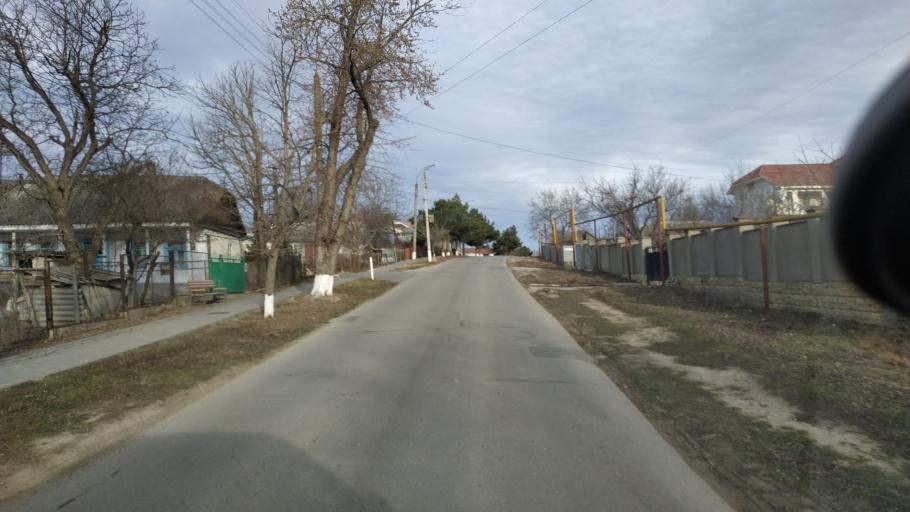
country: MD
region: Chisinau
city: Vadul lui Voda
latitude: 47.0944
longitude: 29.0728
